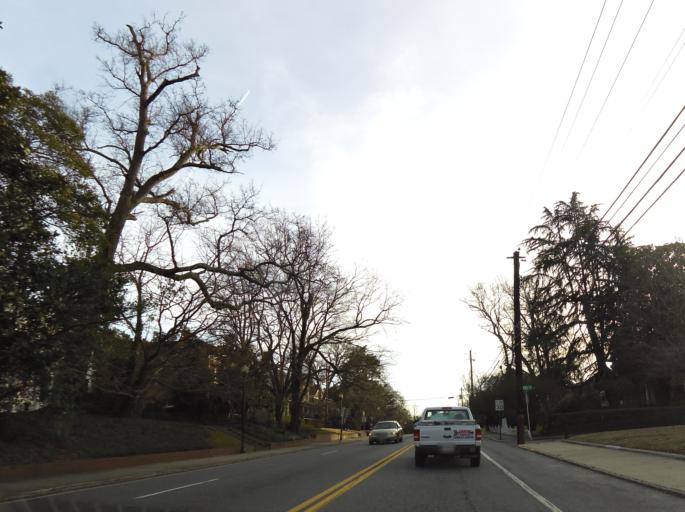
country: US
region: Georgia
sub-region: Bibb County
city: Macon
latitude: 32.8382
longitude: -83.6395
